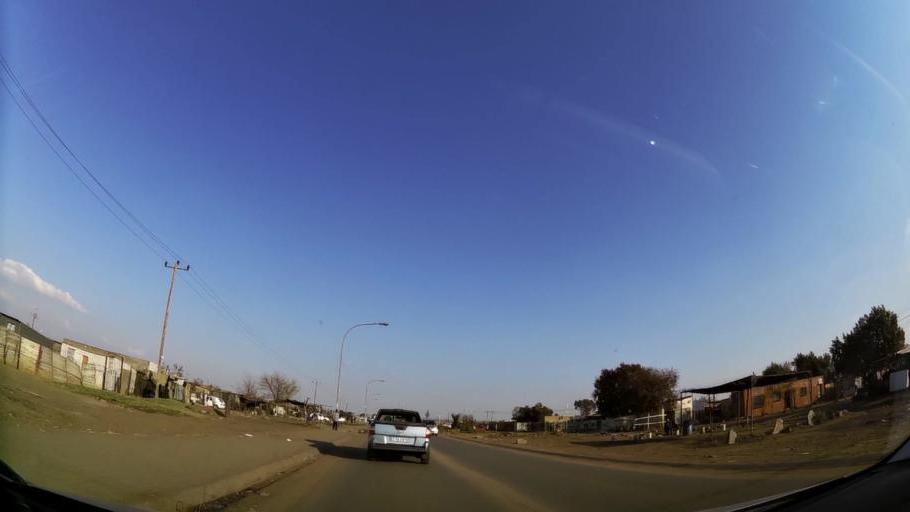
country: ZA
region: Gauteng
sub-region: Ekurhuleni Metropolitan Municipality
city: Tembisa
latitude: -25.9790
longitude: 28.2119
